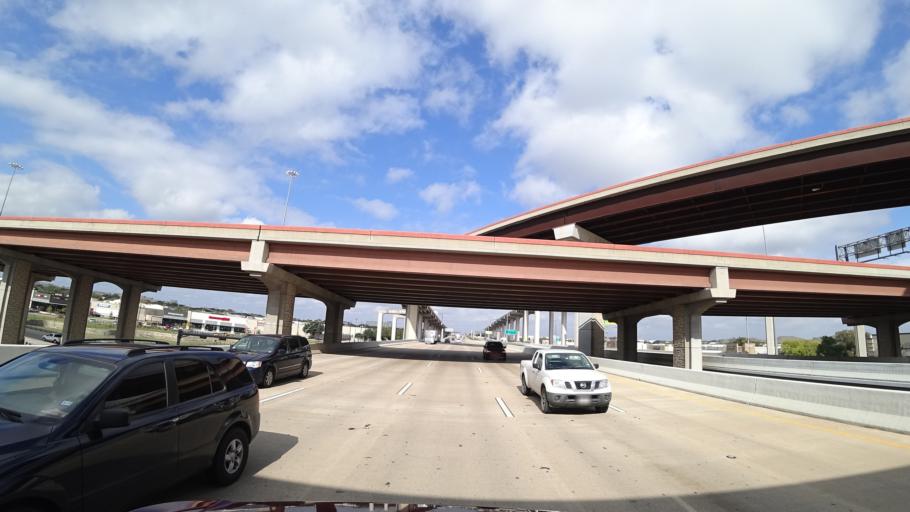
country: US
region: Texas
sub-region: Williamson County
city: Anderson Mill
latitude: 30.4685
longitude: -97.7972
